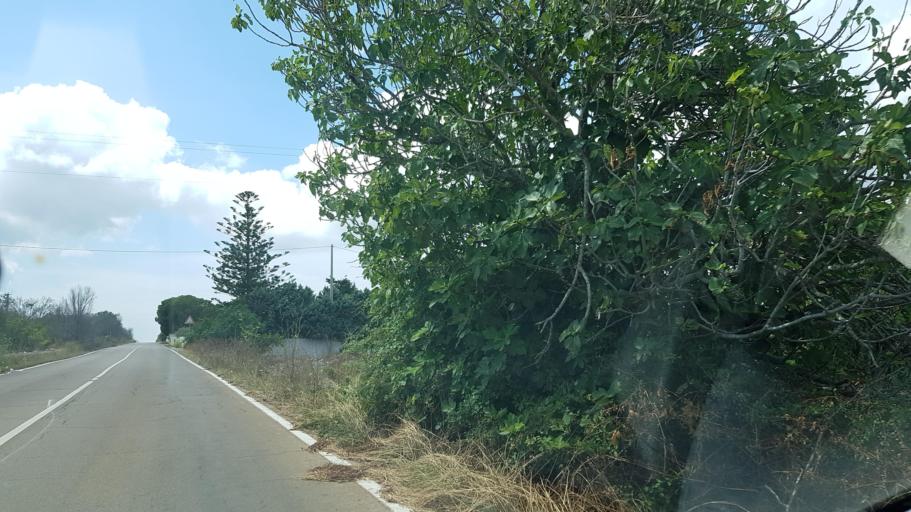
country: IT
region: Apulia
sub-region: Provincia di Lecce
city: Patu
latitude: 39.8449
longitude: 18.3277
